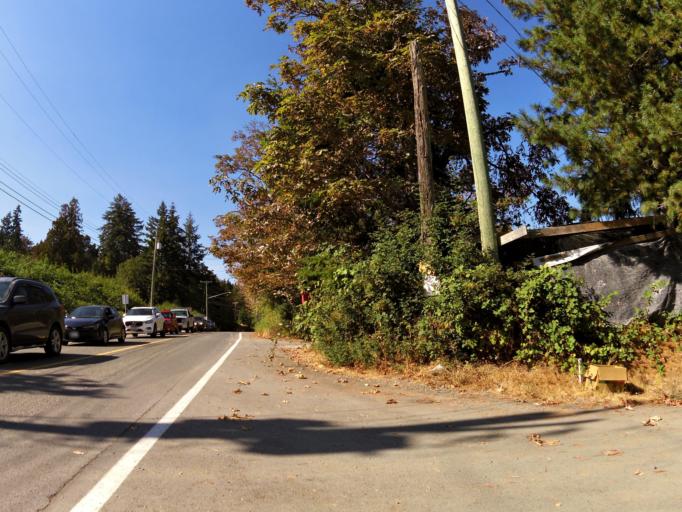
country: CA
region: British Columbia
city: North Saanich
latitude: 48.6147
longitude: -123.5196
